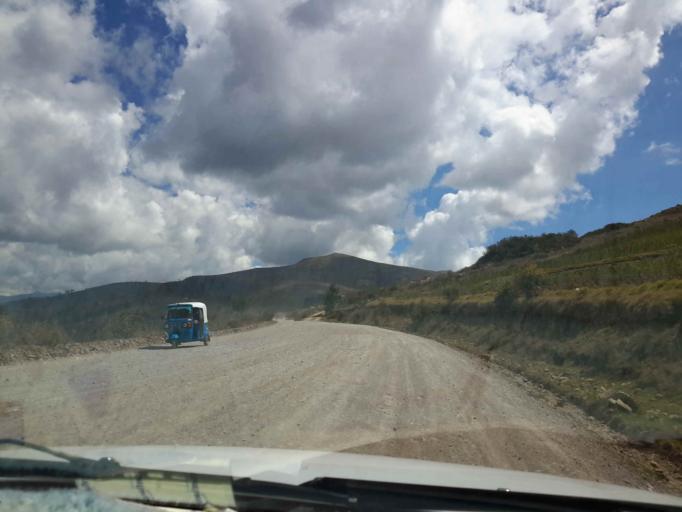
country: PE
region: Apurimac
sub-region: Provincia de Andahuaylas
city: San Jeronimo
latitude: -13.6381
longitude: -73.3378
